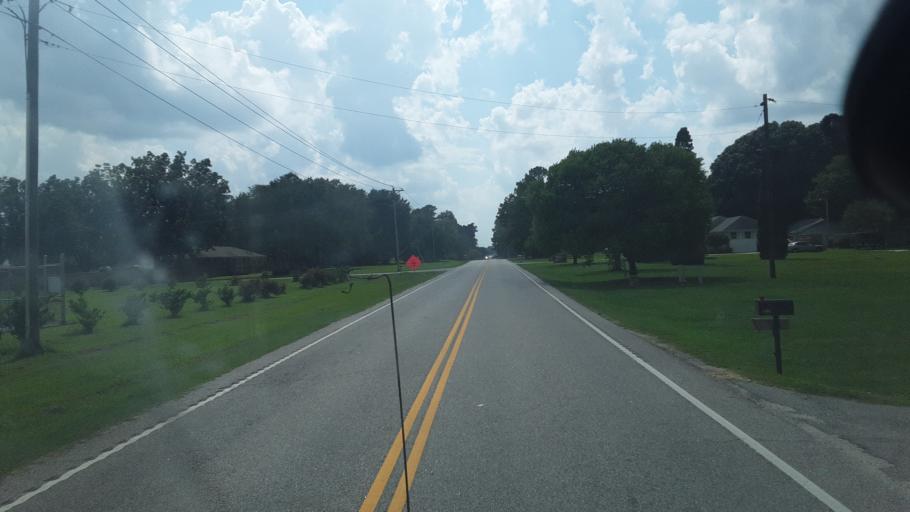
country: US
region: South Carolina
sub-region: Sumter County
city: Sumter
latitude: 33.9618
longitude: -80.3734
